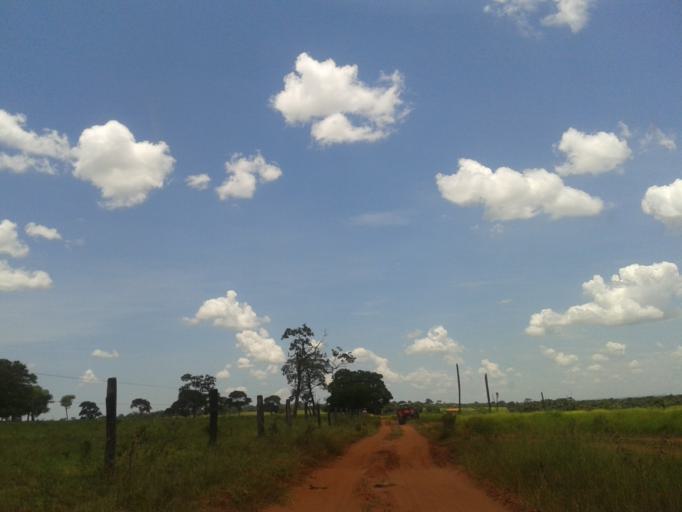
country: BR
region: Minas Gerais
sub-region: Santa Vitoria
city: Santa Vitoria
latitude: -19.2133
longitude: -50.4117
